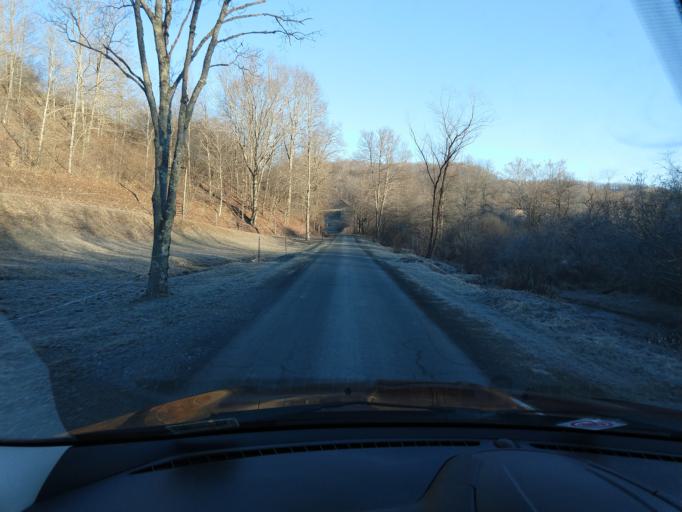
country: US
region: West Virginia
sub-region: Greenbrier County
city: Rainelle
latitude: 37.8980
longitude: -80.7324
